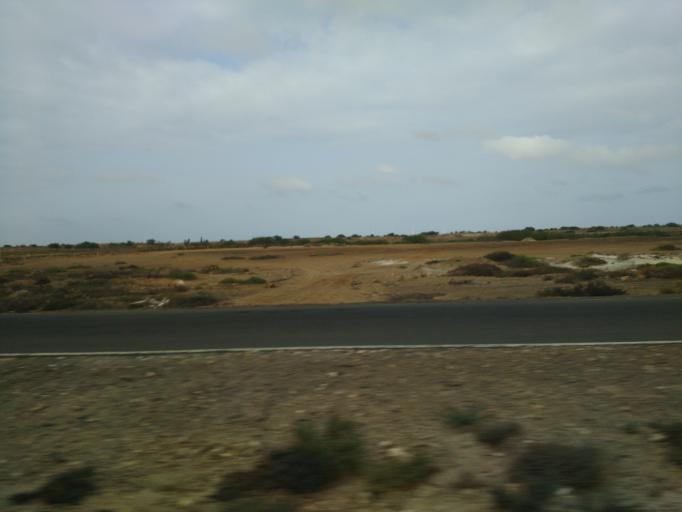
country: CV
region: Sal
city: Espargos
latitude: 16.6945
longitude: -22.9411
